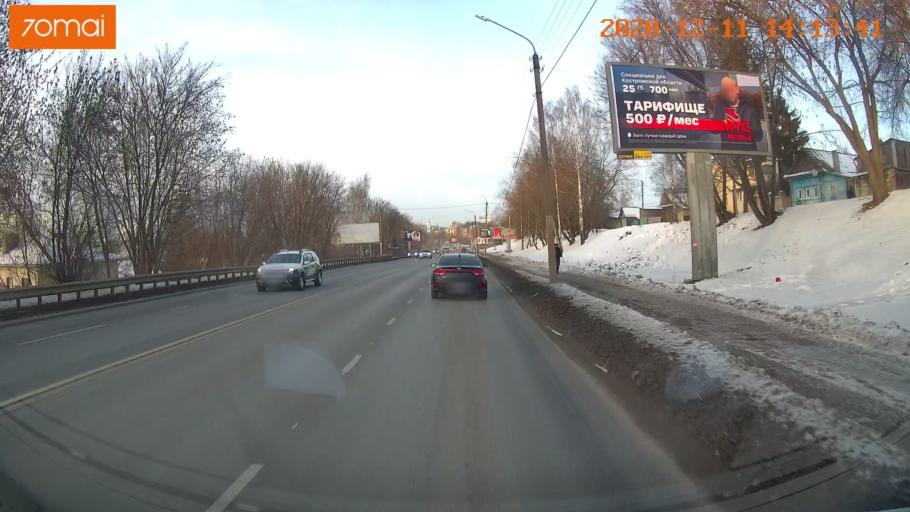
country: RU
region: Kostroma
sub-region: Kostromskoy Rayon
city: Kostroma
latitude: 57.7472
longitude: 40.9568
